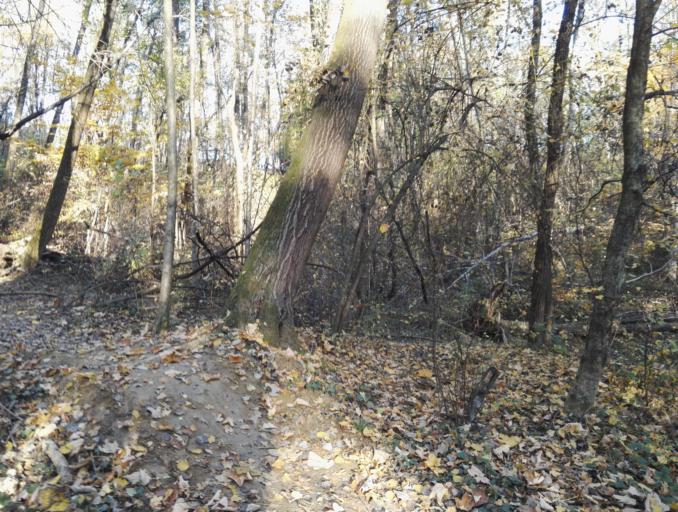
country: AT
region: Styria
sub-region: Graz Stadt
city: Graz
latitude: 47.0607
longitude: 15.4803
